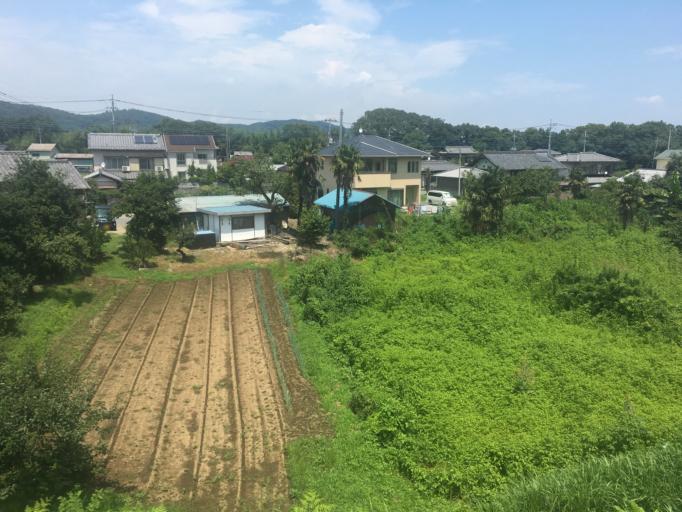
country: JP
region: Saitama
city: Yorii
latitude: 36.1088
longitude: 139.1857
